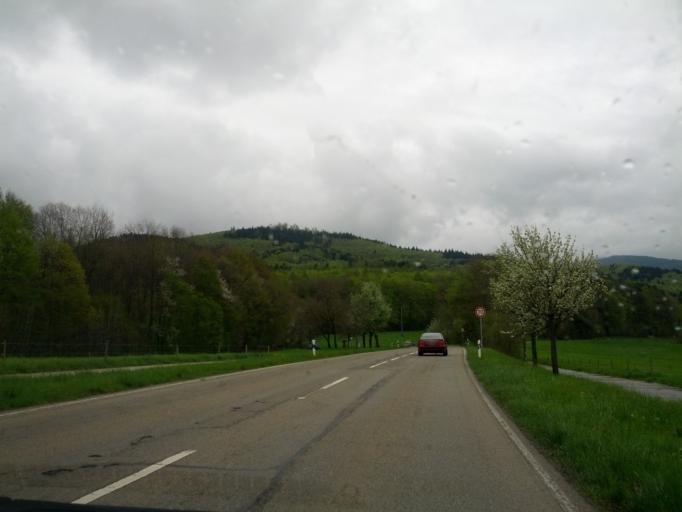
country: DE
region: Baden-Wuerttemberg
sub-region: Freiburg Region
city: Bollschweil
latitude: 47.9237
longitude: 7.7996
